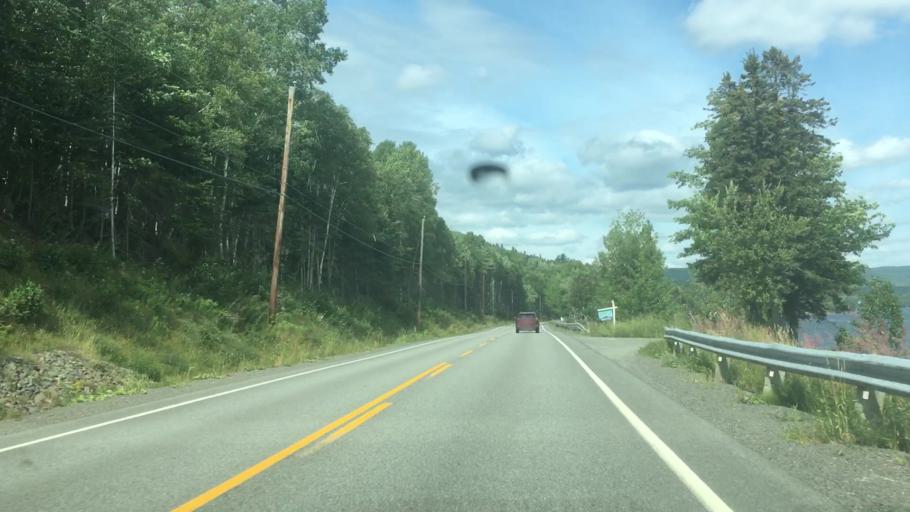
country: CA
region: Nova Scotia
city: Sydney Mines
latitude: 46.2745
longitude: -60.6109
